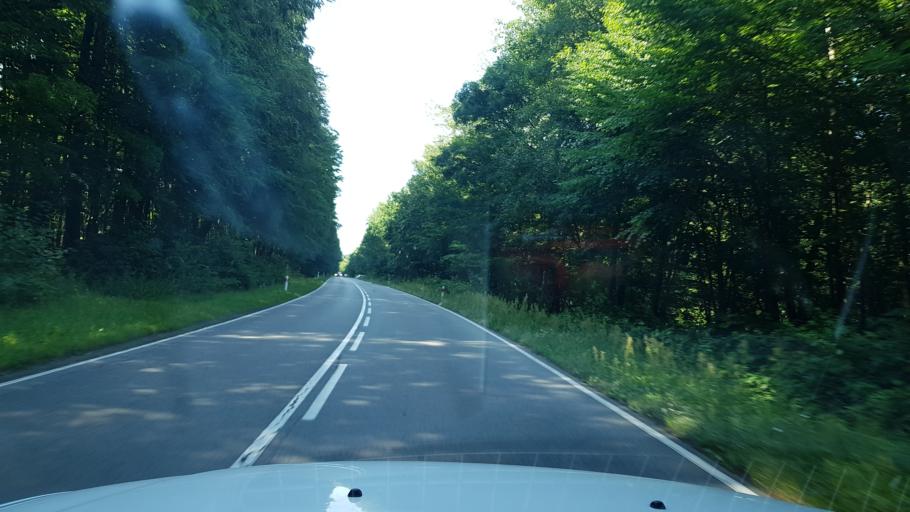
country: PL
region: West Pomeranian Voivodeship
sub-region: Powiat gryfinski
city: Stare Czarnowo
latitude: 53.3198
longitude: 14.7909
